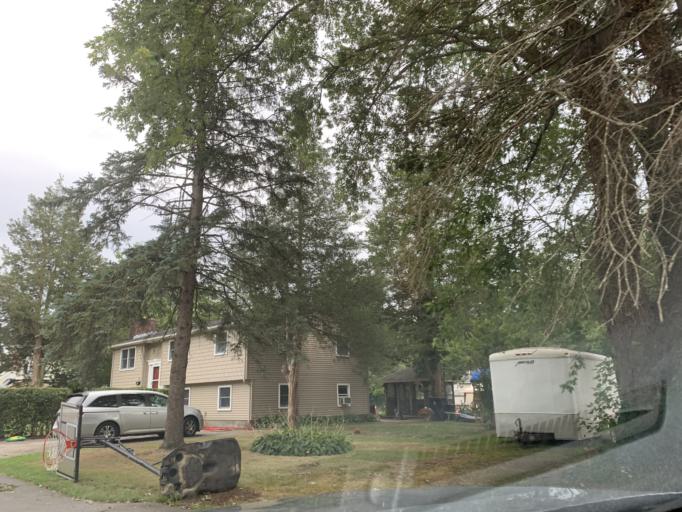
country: US
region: Rhode Island
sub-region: Kent County
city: East Greenwich
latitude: 41.6358
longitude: -71.4612
